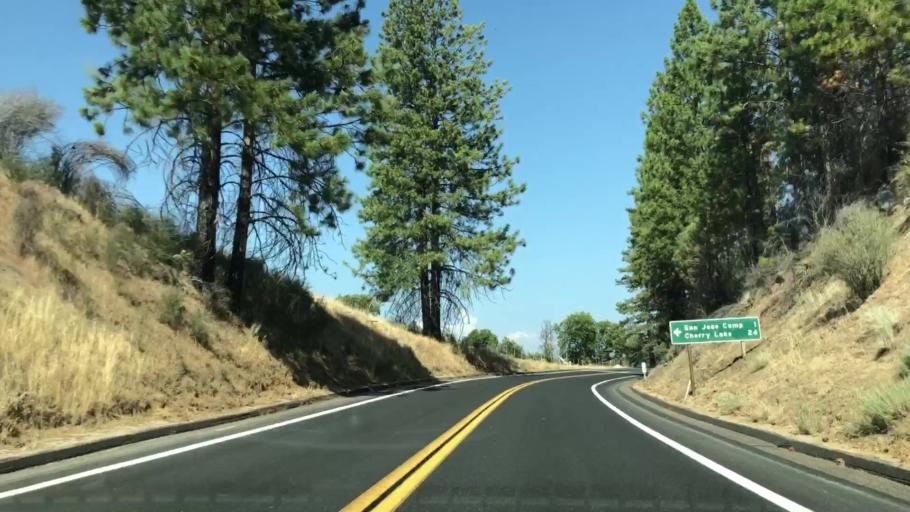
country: US
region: California
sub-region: Tuolumne County
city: Tuolumne City
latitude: 37.8242
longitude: -120.0121
